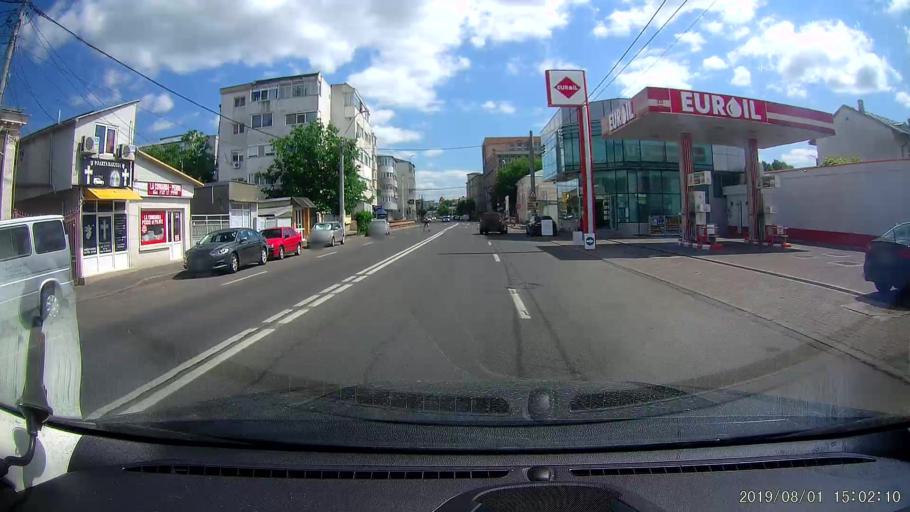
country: RO
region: Braila
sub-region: Municipiul Braila
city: Braila
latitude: 45.2673
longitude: 27.9611
